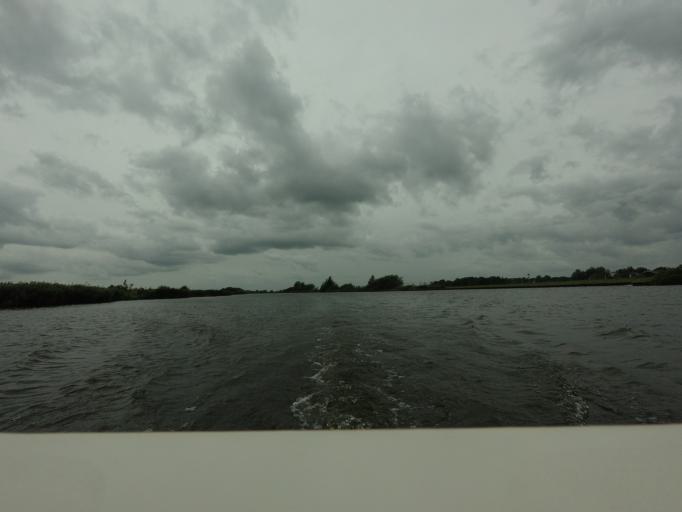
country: NL
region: Friesland
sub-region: Gemeente Boarnsterhim
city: Warten
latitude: 53.1011
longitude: 5.9113
